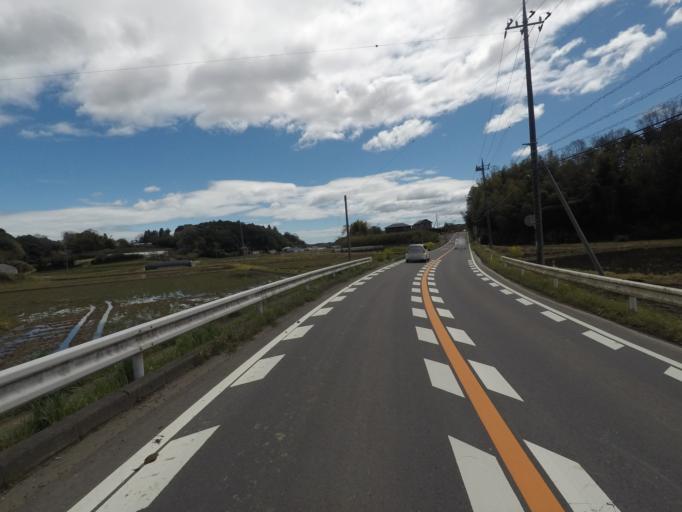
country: JP
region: Ibaraki
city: Itako
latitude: 36.1065
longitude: 140.4793
